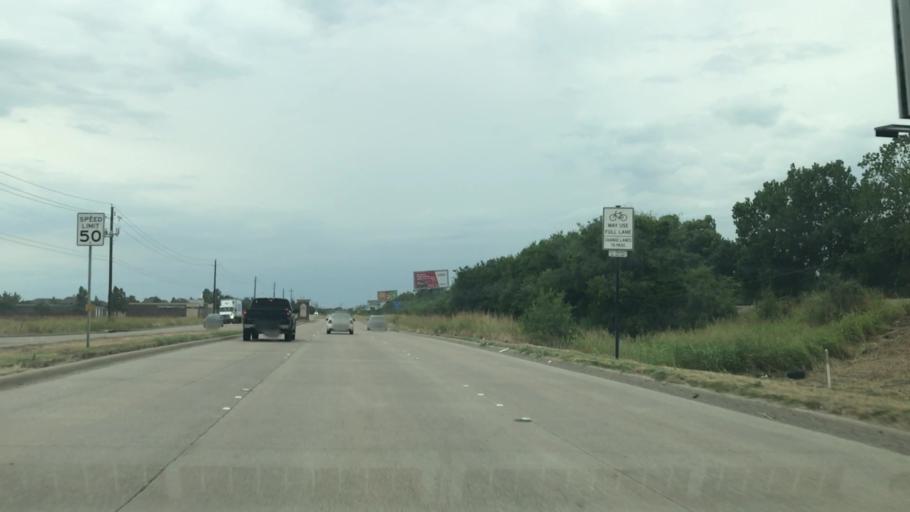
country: US
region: Texas
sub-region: Dallas County
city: Carrollton
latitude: 32.9517
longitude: -96.9408
